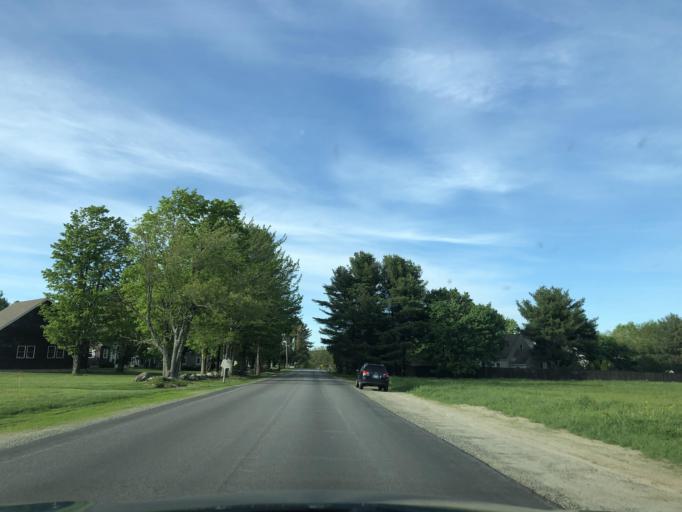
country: US
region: New Hampshire
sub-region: Merrimack County
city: New London
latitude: 43.4259
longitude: -71.9974
